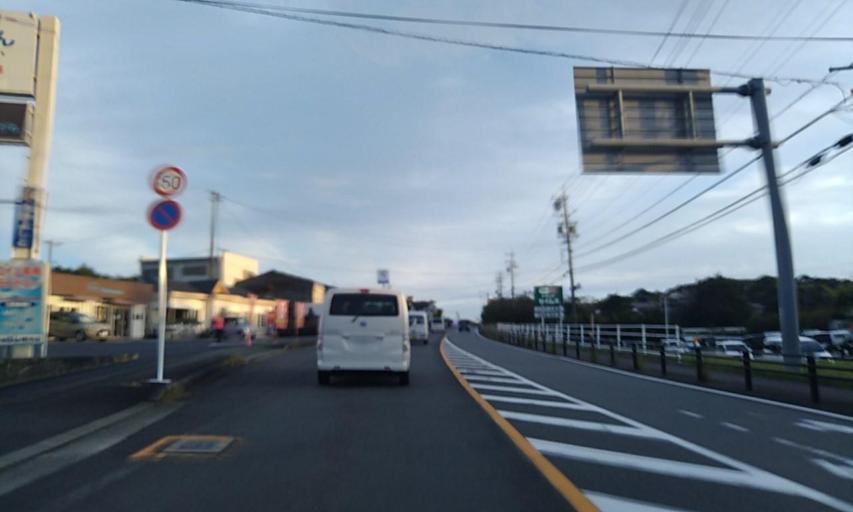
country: JP
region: Mie
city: Toba
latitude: 34.3280
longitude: 136.8397
